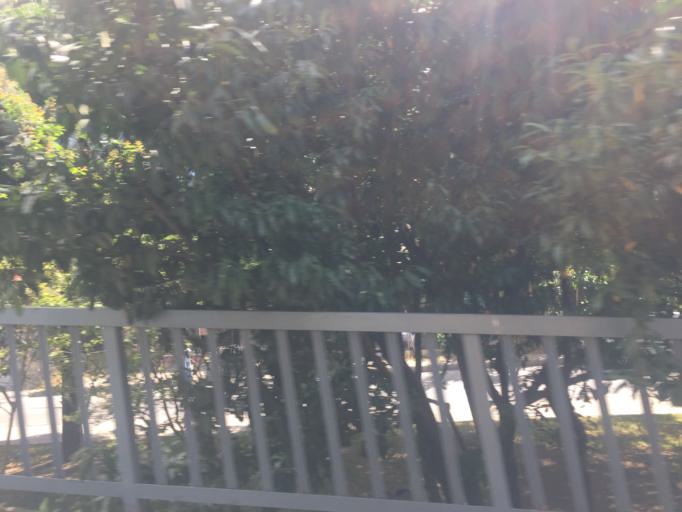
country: TR
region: Istanbul
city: merter keresteciler
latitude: 41.0312
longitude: 28.9143
